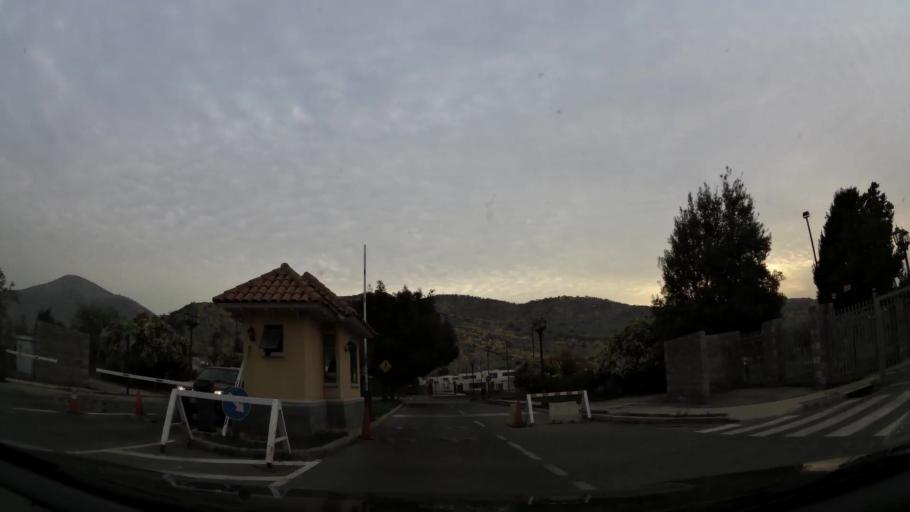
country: CL
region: Santiago Metropolitan
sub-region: Provincia de Chacabuco
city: Chicureo Abajo
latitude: -33.3108
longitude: -70.6574
